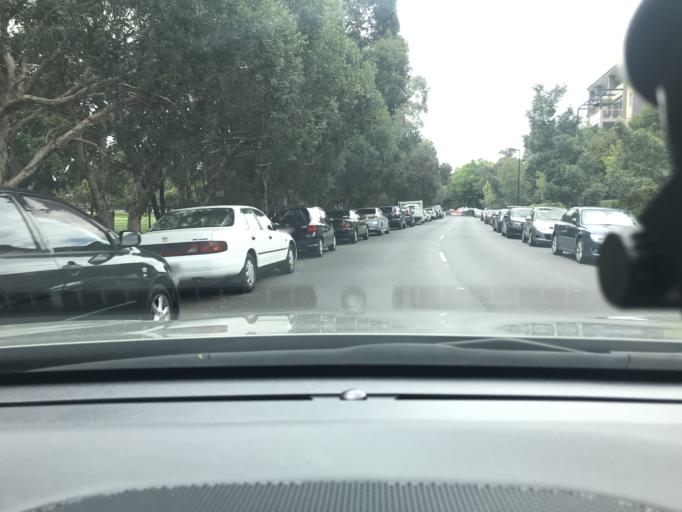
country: AU
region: New South Wales
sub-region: Canada Bay
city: Wareemba
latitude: -33.8671
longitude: 151.1193
